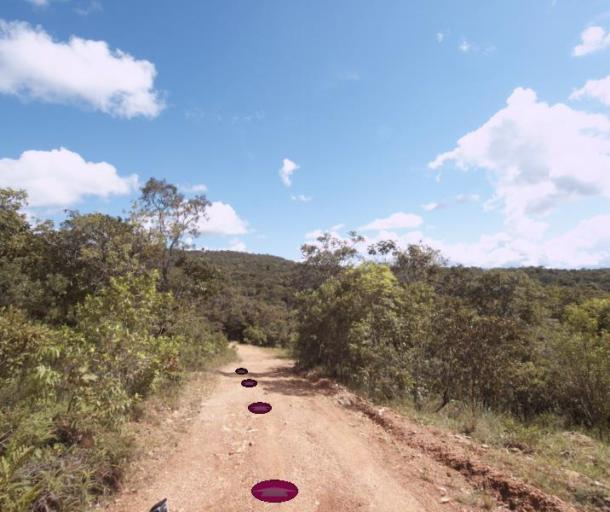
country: BR
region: Goias
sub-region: Pirenopolis
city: Pirenopolis
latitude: -15.7752
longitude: -48.9850
